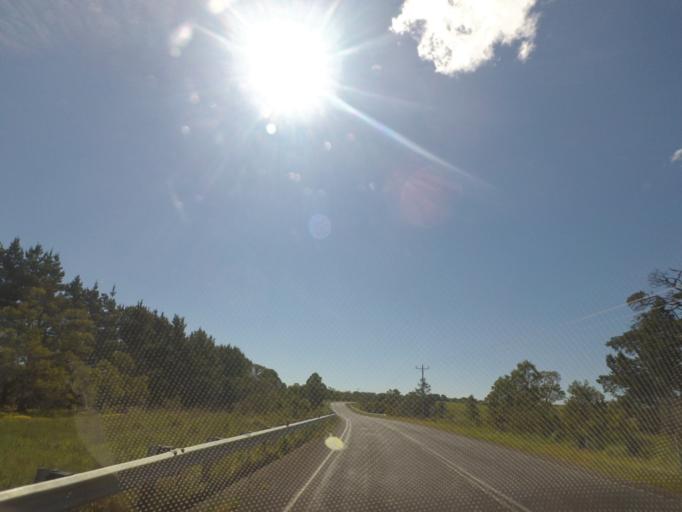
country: AU
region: Victoria
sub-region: Moorabool
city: Bacchus Marsh
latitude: -37.6418
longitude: 144.2240
